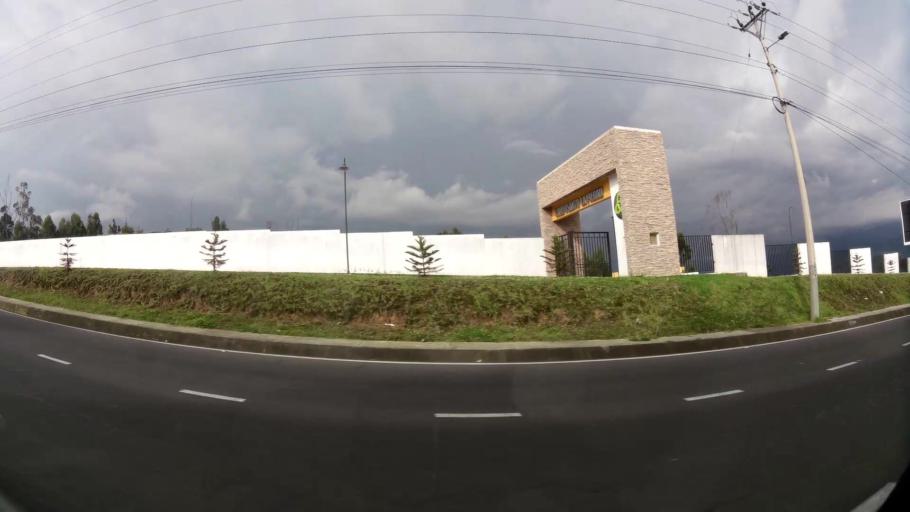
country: EC
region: Pichincha
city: Sangolqui
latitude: -0.3498
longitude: -78.5229
